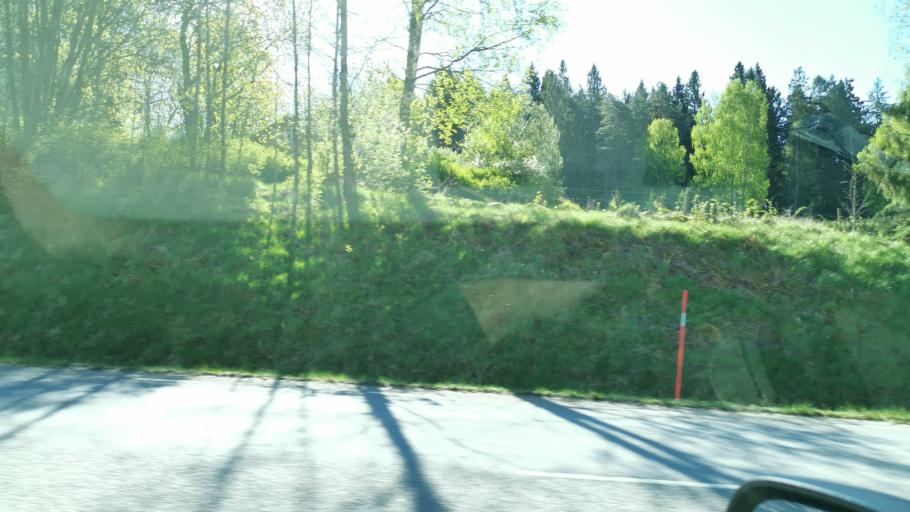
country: SE
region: Vaestra Goetaland
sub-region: Uddevalla Kommun
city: Ljungskile
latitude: 58.2877
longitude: 11.8944
